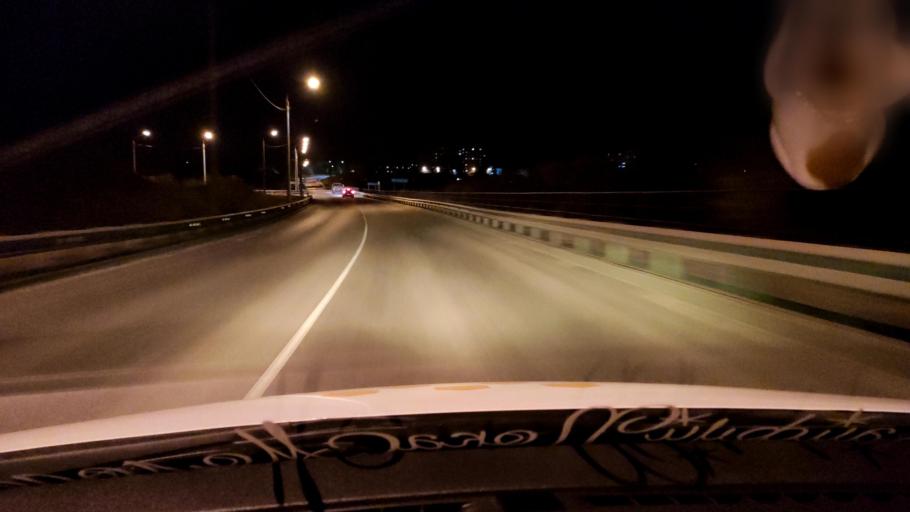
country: RU
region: Voronezj
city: Semiluki
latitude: 51.6732
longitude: 39.0340
